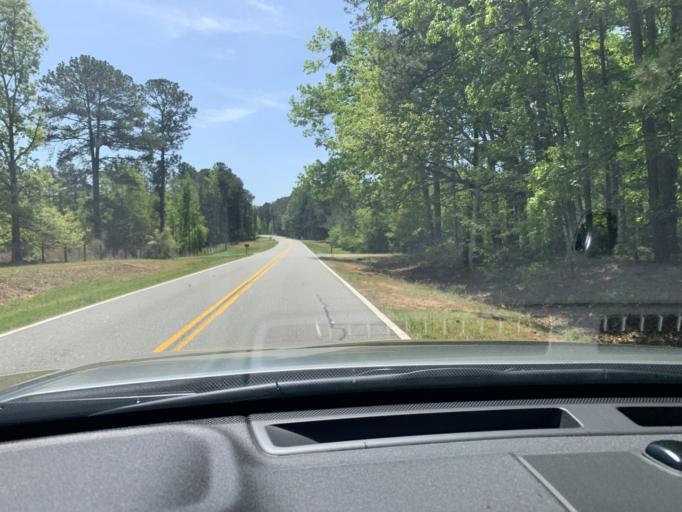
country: US
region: Georgia
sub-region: Oconee County
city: Bogart
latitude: 33.8728
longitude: -83.5549
